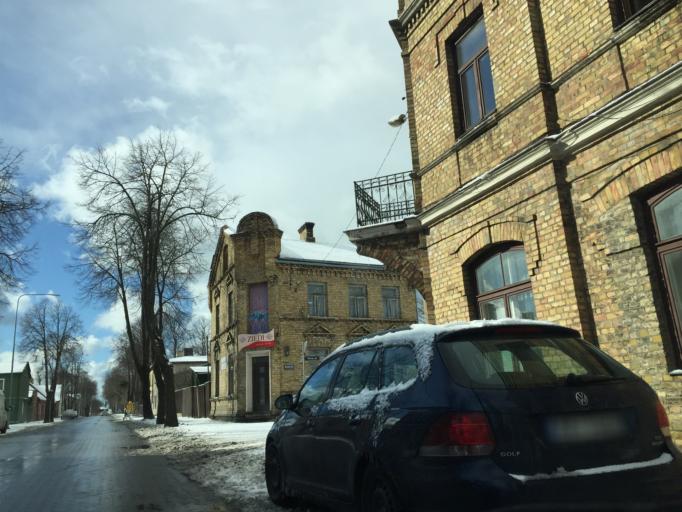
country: LV
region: Ventspils
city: Ventspils
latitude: 57.3920
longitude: 21.5579
